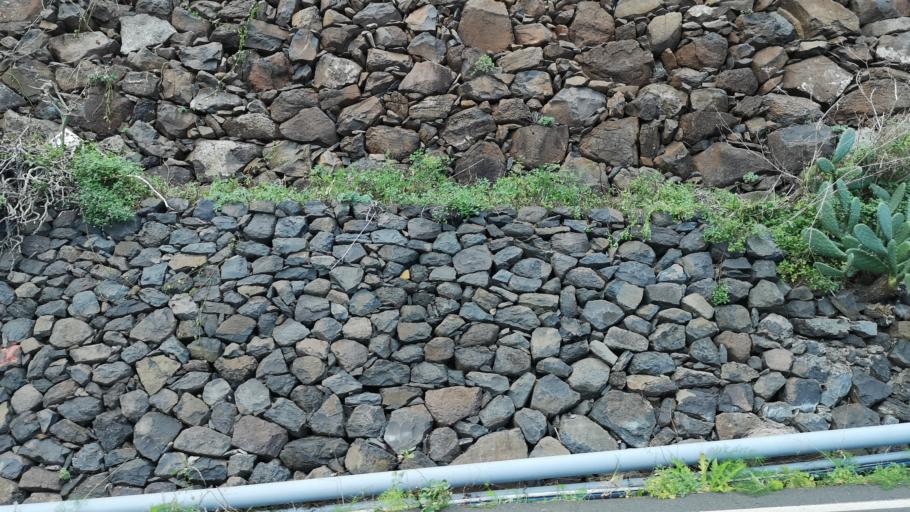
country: ES
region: Canary Islands
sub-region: Provincia de Santa Cruz de Tenerife
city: Agulo
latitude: 28.1880
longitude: -17.1978
